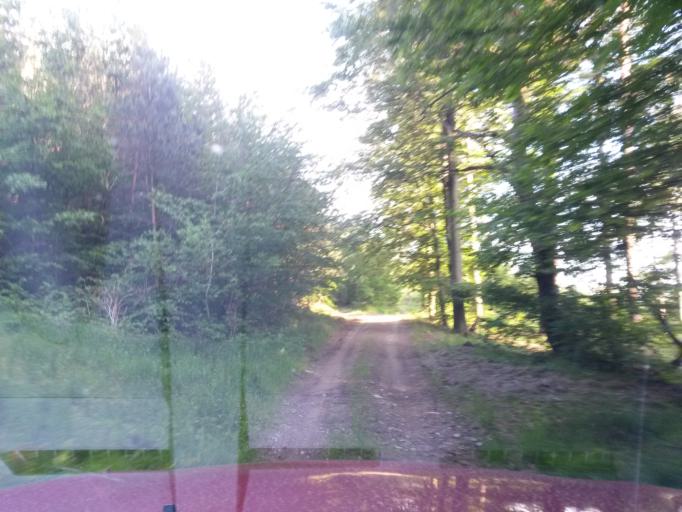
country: SK
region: Kosicky
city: Moldava nad Bodvou
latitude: 48.7380
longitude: 21.0379
